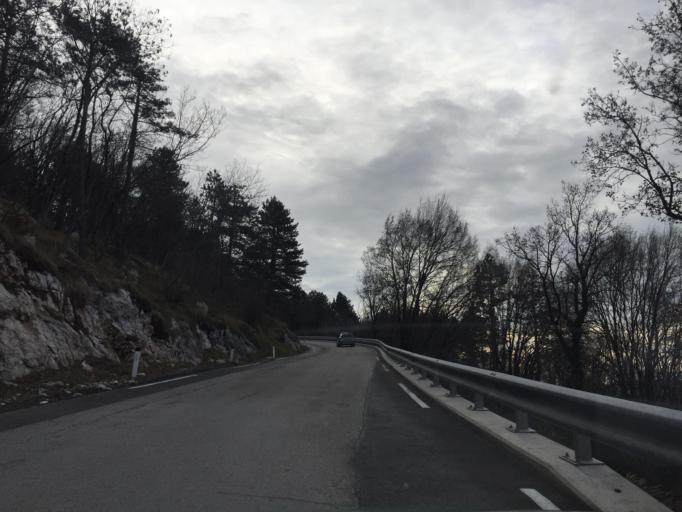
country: SI
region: Nova Gorica
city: Sempas
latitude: 45.9729
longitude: 13.7217
